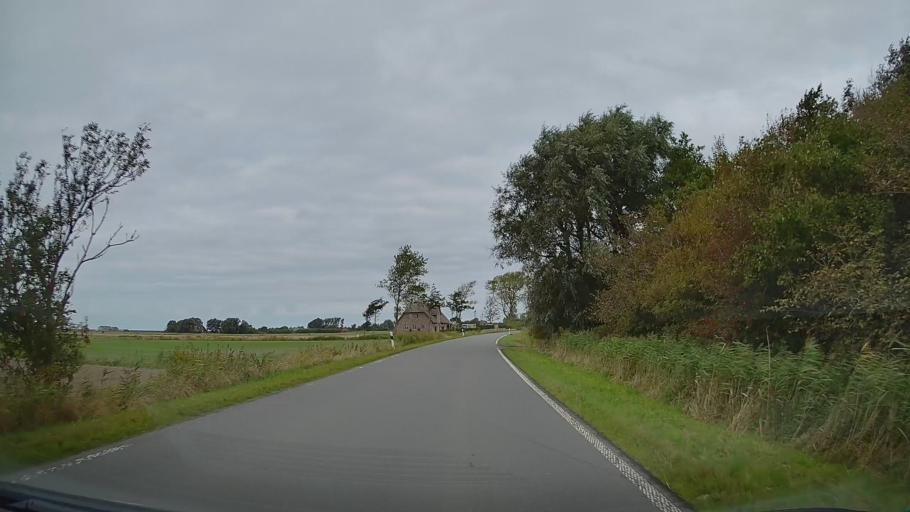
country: DE
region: Schleswig-Holstein
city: Klanxbull
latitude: 54.8780
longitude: 8.6817
